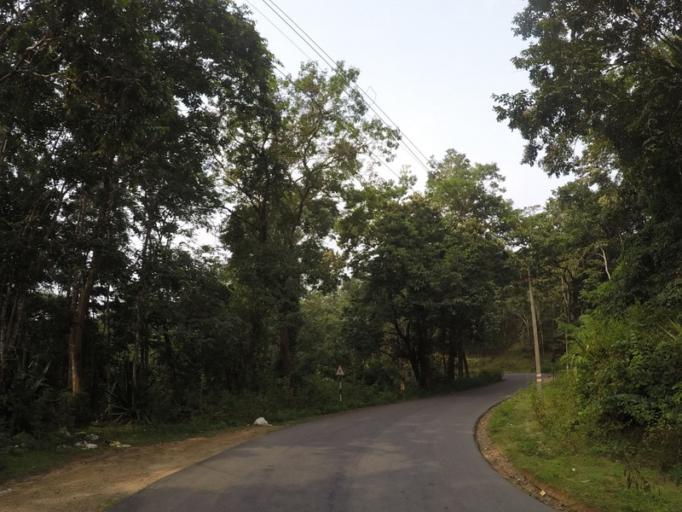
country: IN
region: Karnataka
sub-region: Chikmagalur
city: Koppa
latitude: 13.3601
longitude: 75.5017
